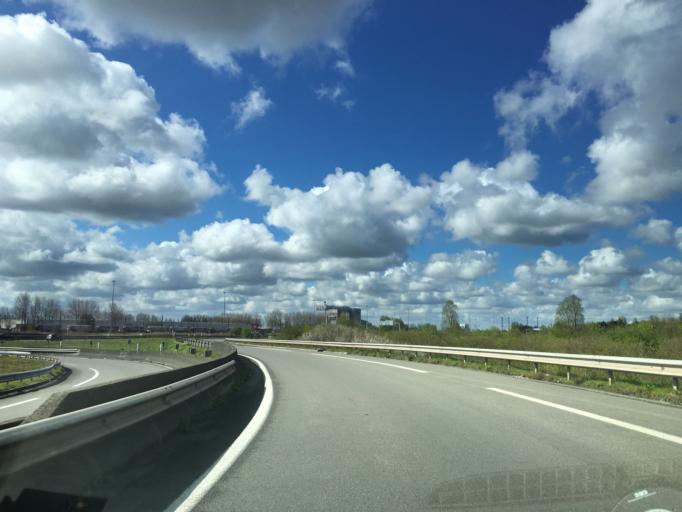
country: FR
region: Nord-Pas-de-Calais
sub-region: Departement du Nord
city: Grande-Synthe
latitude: 51.0082
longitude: 2.3229
